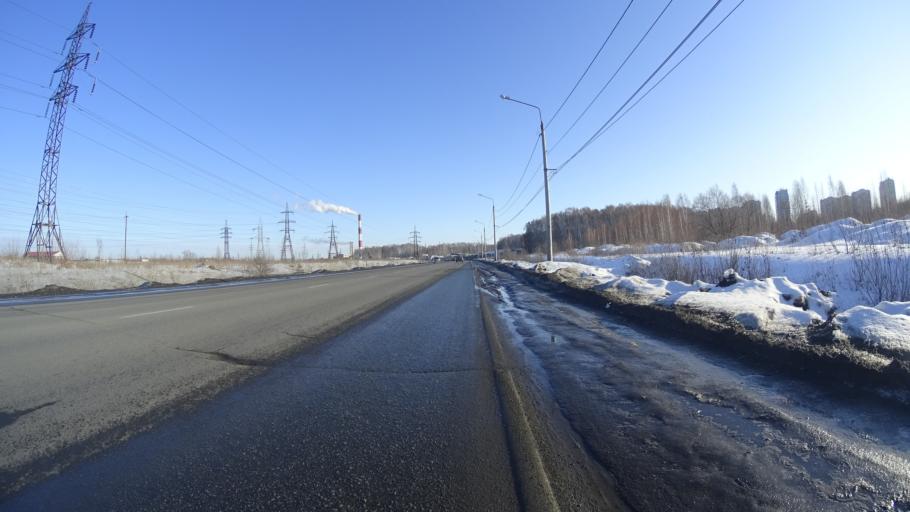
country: RU
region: Chelyabinsk
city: Roshchino
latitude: 55.2133
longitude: 61.3064
